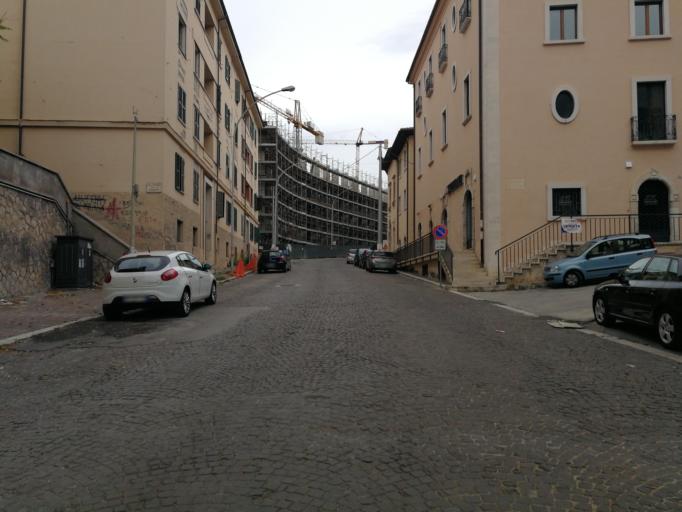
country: IT
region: Abruzzo
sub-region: Provincia dell' Aquila
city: L'Aquila
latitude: 42.3503
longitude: 13.3931
